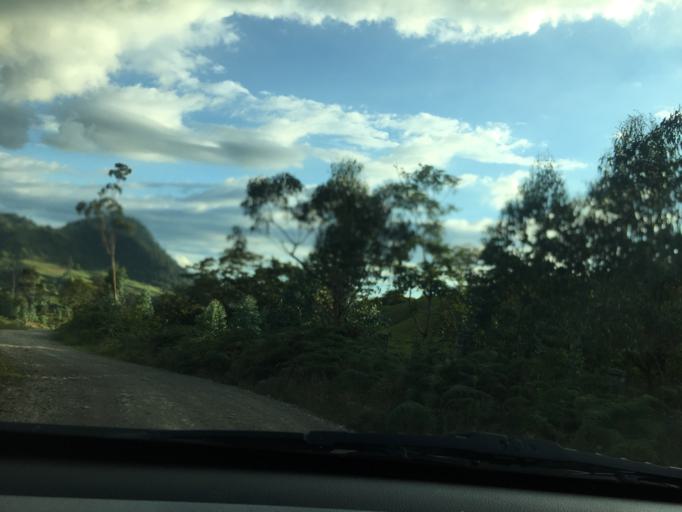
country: CO
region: Cundinamarca
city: Zipacon
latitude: 4.7309
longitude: -74.3907
